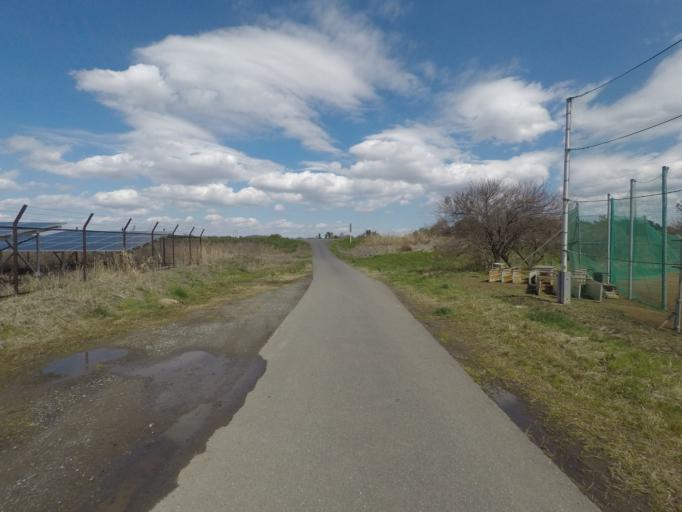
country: JP
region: Ibaraki
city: Fujishiro
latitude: 35.9398
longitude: 140.1240
